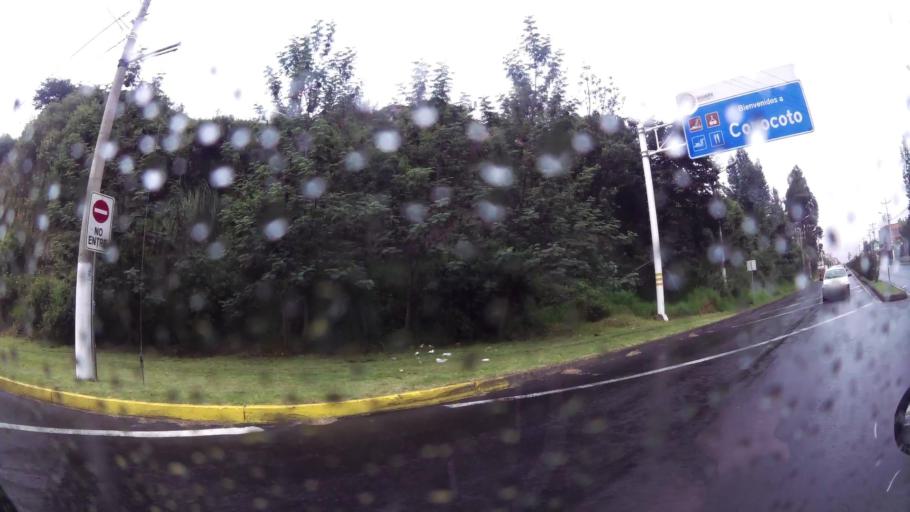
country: EC
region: Pichincha
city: Sangolqui
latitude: -0.2843
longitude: -78.4716
